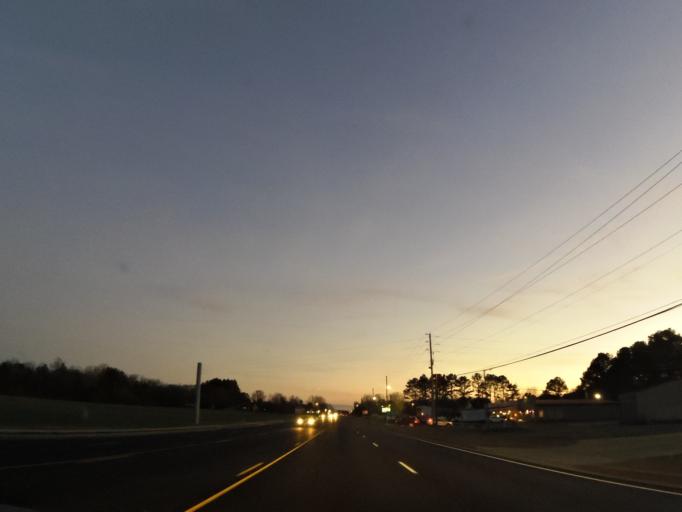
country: US
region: Georgia
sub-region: Whitfield County
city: Varnell
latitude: 34.8825
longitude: -84.9456
